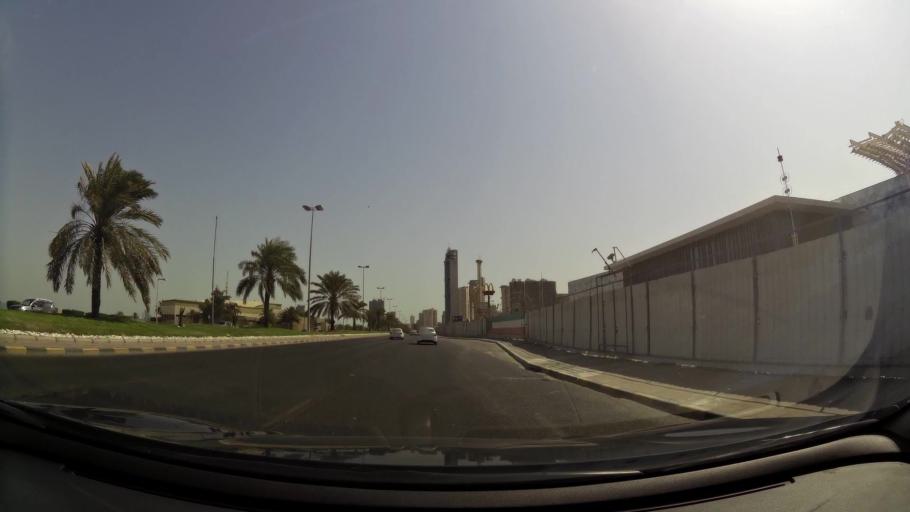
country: KW
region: Muhafazat Hawalli
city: Hawalli
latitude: 29.3454
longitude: 48.0417
